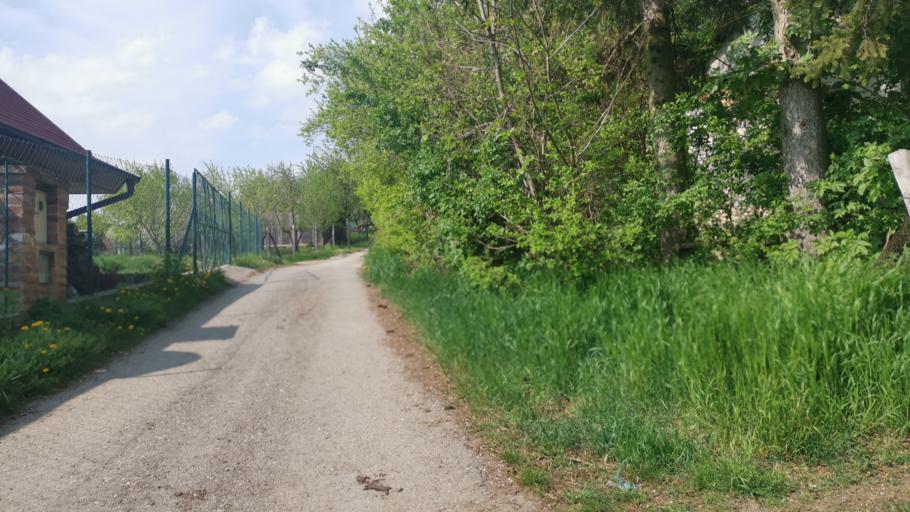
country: SK
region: Trnavsky
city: Smolenice
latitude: 48.5615
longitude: 17.3497
